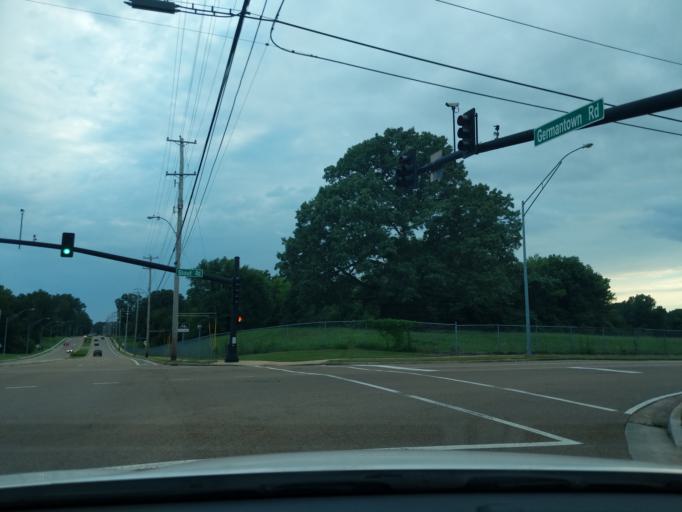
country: US
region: Tennessee
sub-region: Shelby County
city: Germantown
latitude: 35.0776
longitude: -89.8123
